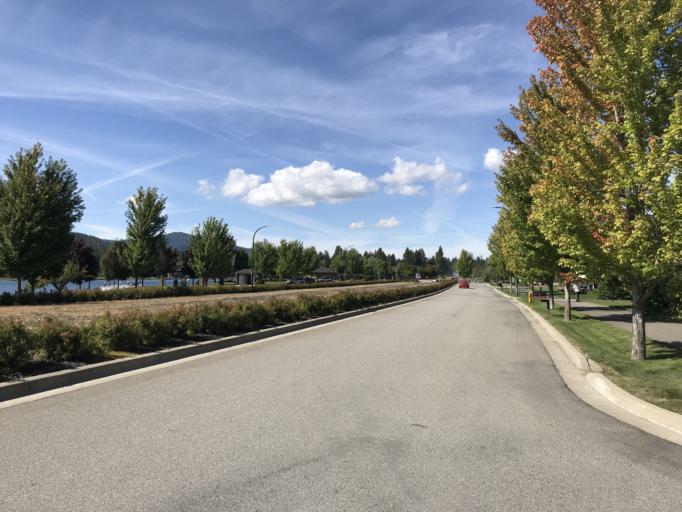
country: US
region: Idaho
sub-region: Kootenai County
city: Coeur d'Alene
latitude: 47.7011
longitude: -116.8425
